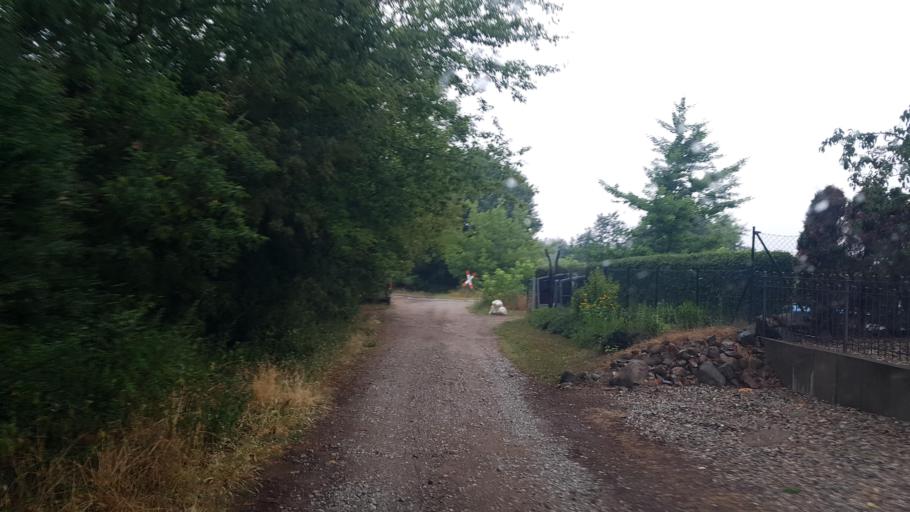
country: DE
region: Brandenburg
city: Juterbog
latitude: 52.0080
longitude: 13.0828
